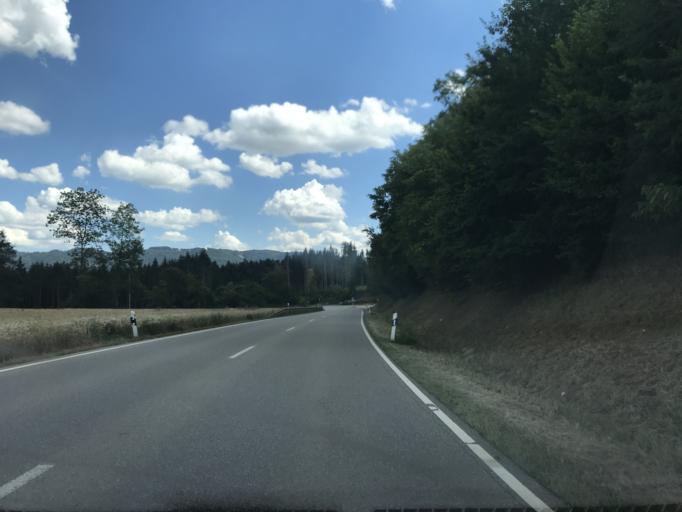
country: DE
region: Baden-Wuerttemberg
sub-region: Freiburg Region
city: Hasel
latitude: 47.6476
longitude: 7.8652
